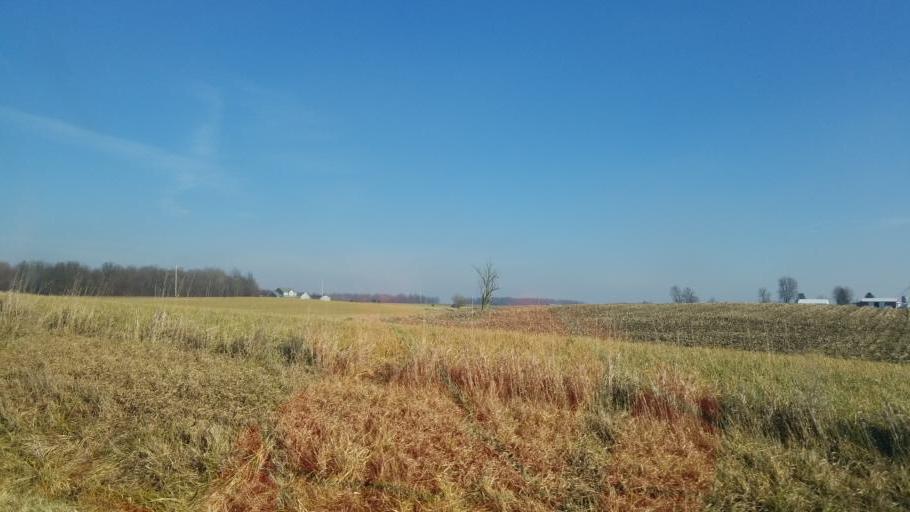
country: US
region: Ohio
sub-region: Seneca County
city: Tiffin
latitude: 40.9920
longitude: -83.0742
